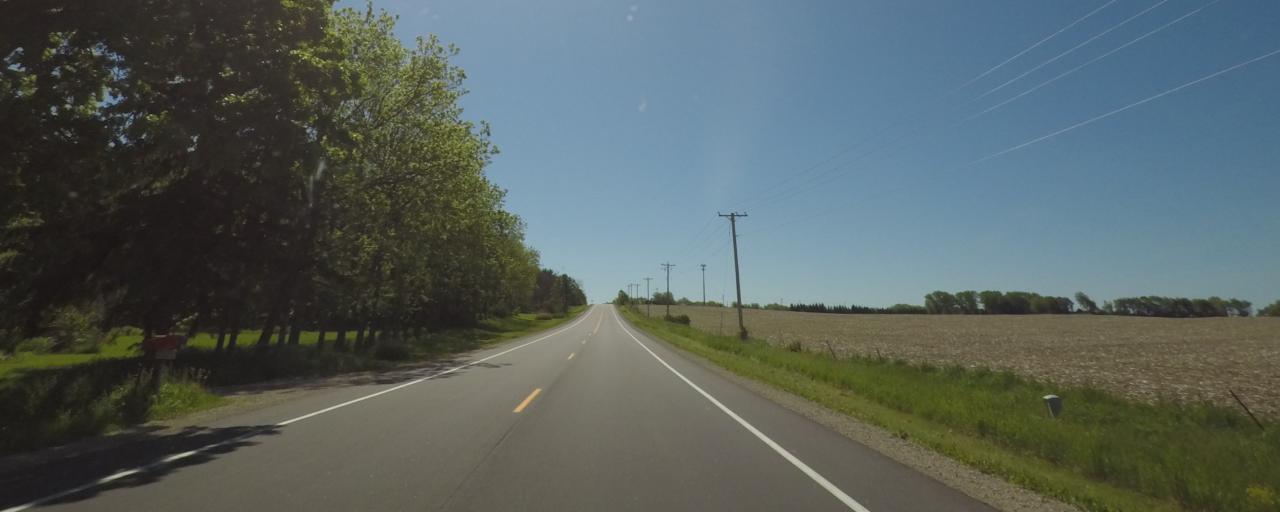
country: US
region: Wisconsin
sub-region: Dane County
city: Fitchburg
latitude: 42.9542
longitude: -89.4662
